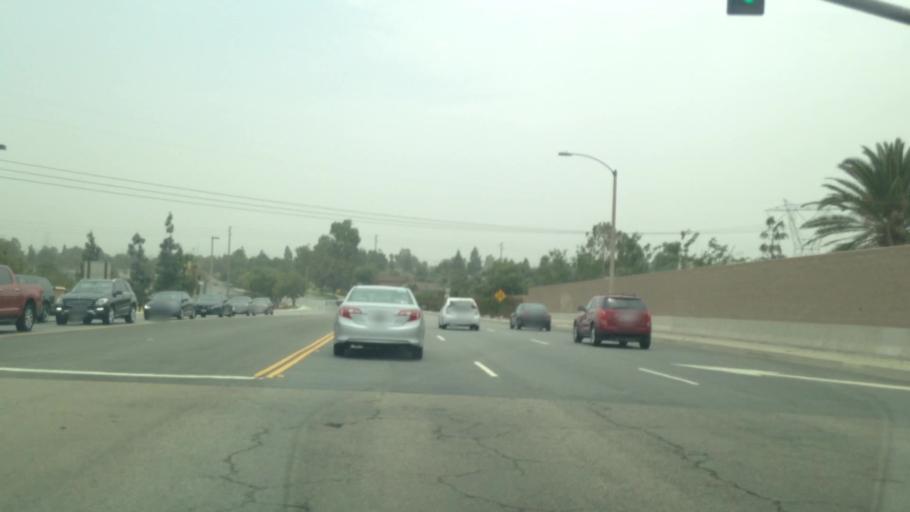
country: US
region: California
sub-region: Riverside County
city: Mira Loma
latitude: 34.0281
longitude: -117.5758
